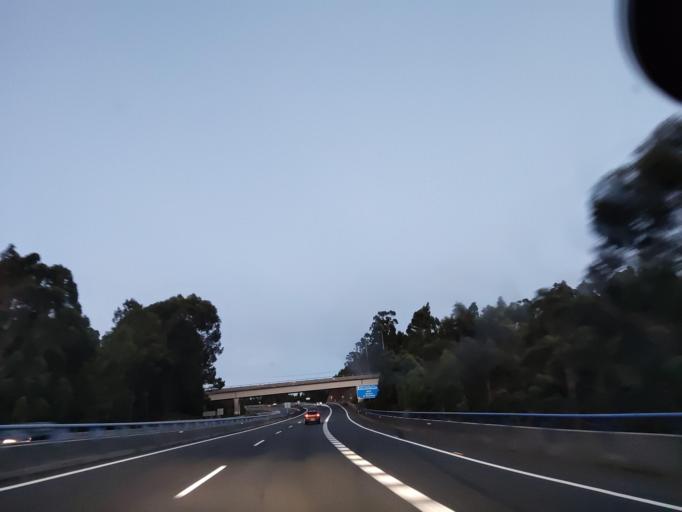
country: ES
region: Galicia
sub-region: Provincia da Coruna
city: Boiro
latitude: 42.6240
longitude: -8.9310
